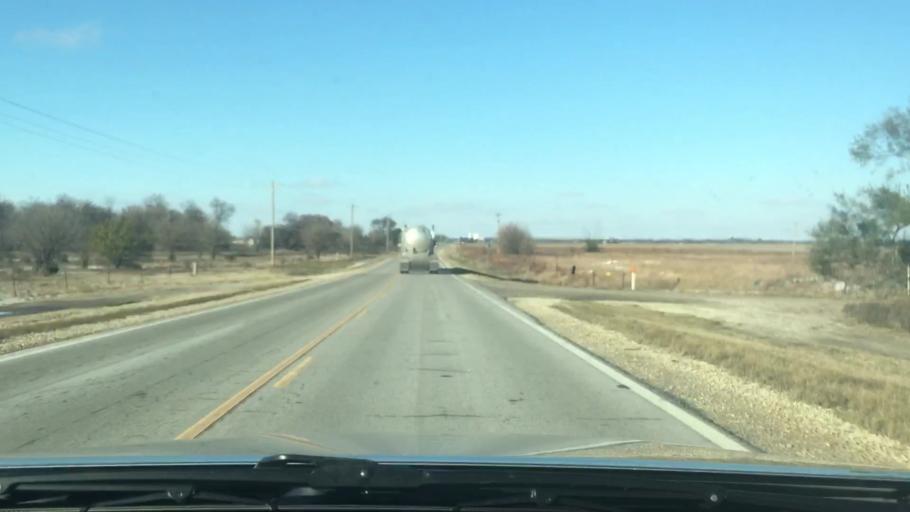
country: US
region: Kansas
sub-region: Rice County
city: Sterling
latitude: 38.1716
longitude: -98.2069
